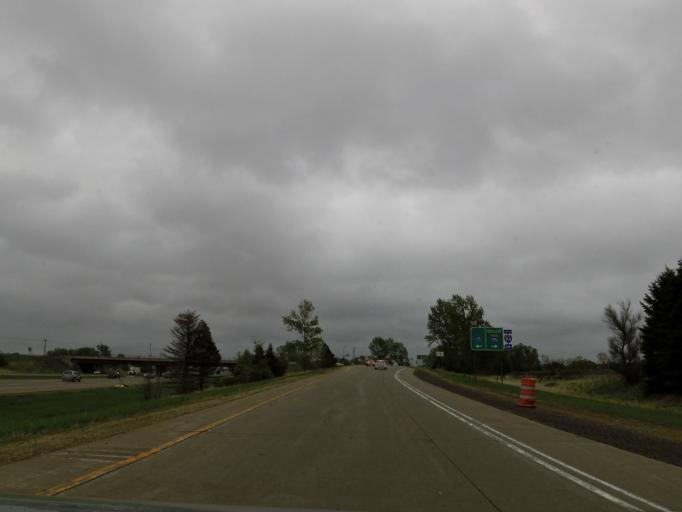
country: US
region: Minnesota
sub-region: Washington County
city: Lake Elmo
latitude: 44.9482
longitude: -92.8660
